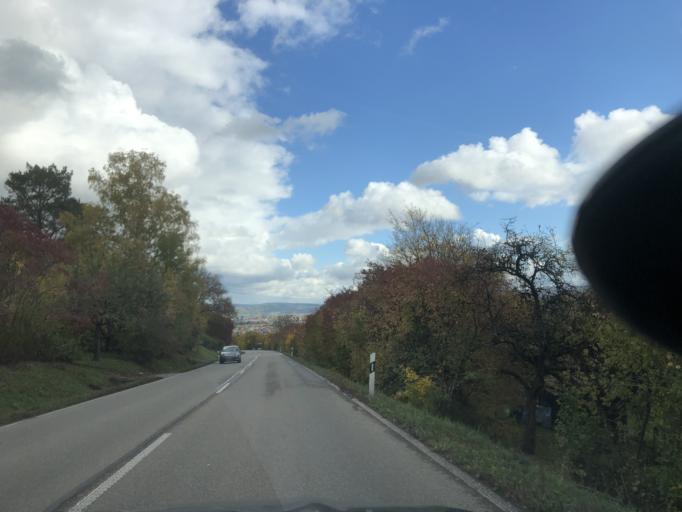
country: DE
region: Baden-Wuerttemberg
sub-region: Regierungsbezirk Stuttgart
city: Winterbach
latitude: 48.7920
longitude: 9.4718
